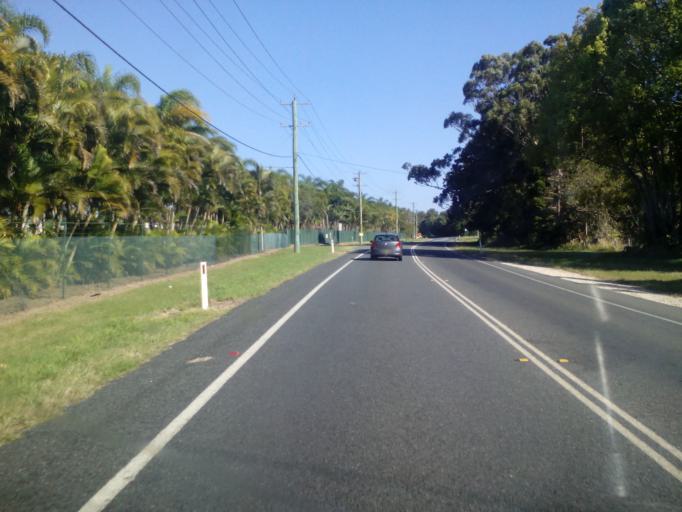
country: AU
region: New South Wales
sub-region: Tweed
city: Kingscliff
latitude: -28.2542
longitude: 153.5596
